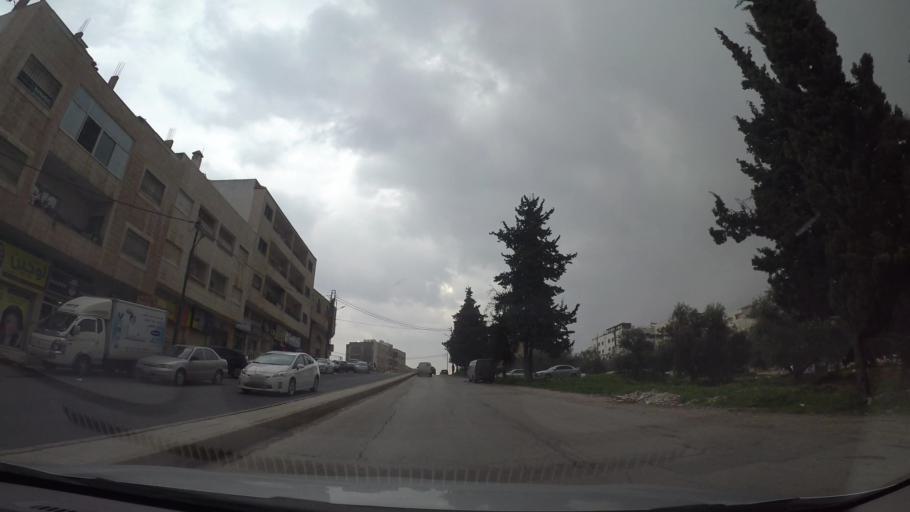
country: JO
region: Amman
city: Umm as Summaq
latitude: 31.8866
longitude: 35.8567
